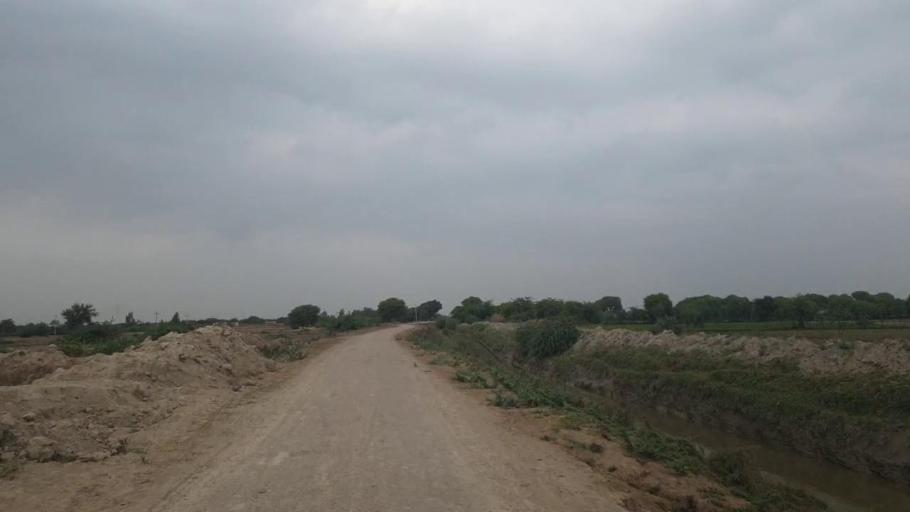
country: PK
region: Sindh
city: Badin
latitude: 24.6295
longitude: 68.6817
